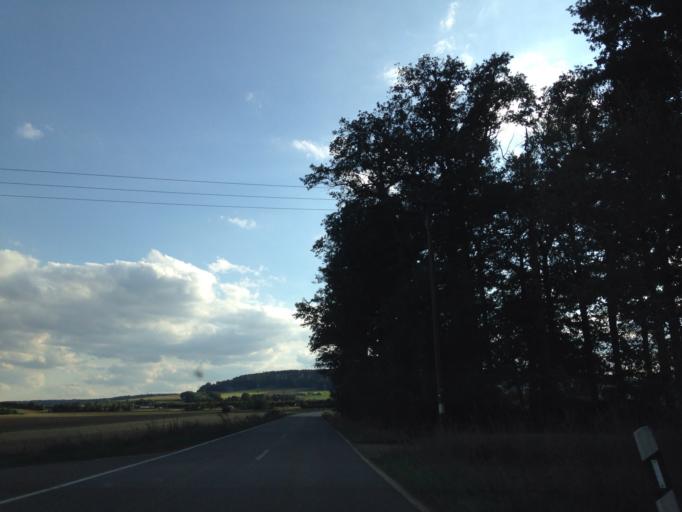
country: DE
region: Bavaria
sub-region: Regierungsbezirk Mittelfranken
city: Thalmassing
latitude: 49.1474
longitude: 11.2725
